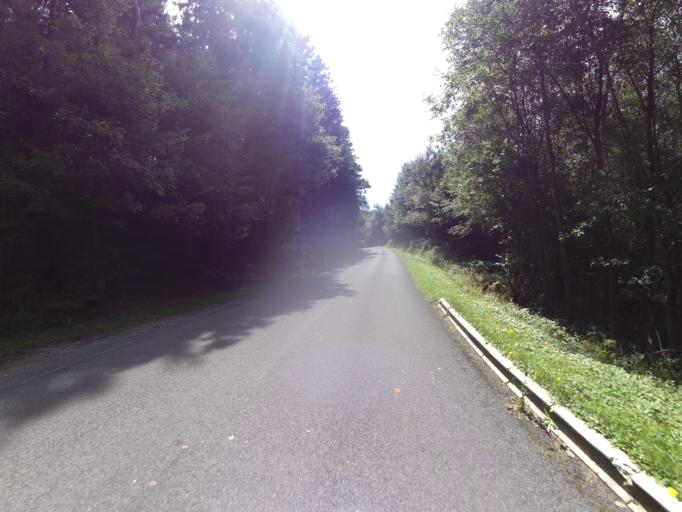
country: BE
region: Wallonia
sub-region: Province du Luxembourg
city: Saint-Hubert
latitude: 50.0408
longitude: 5.3565
